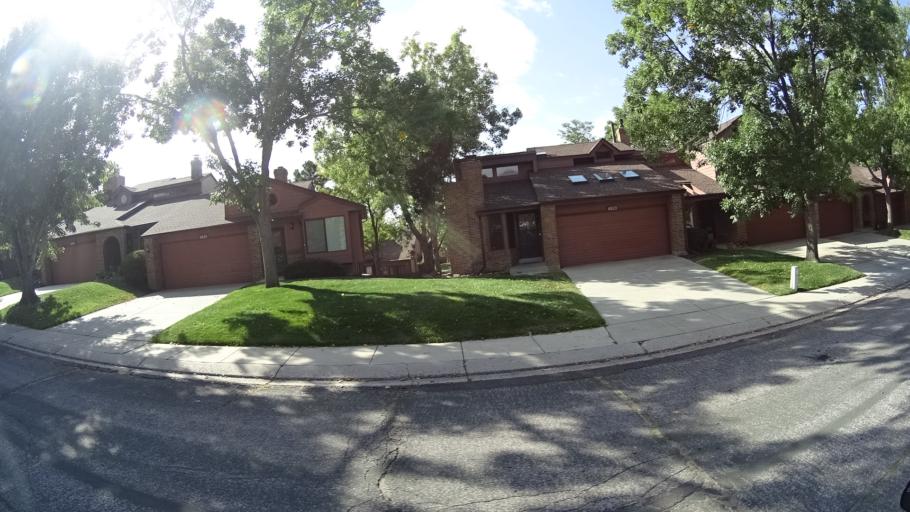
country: US
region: Colorado
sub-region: El Paso County
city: Cimarron Hills
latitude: 38.8838
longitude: -104.7376
